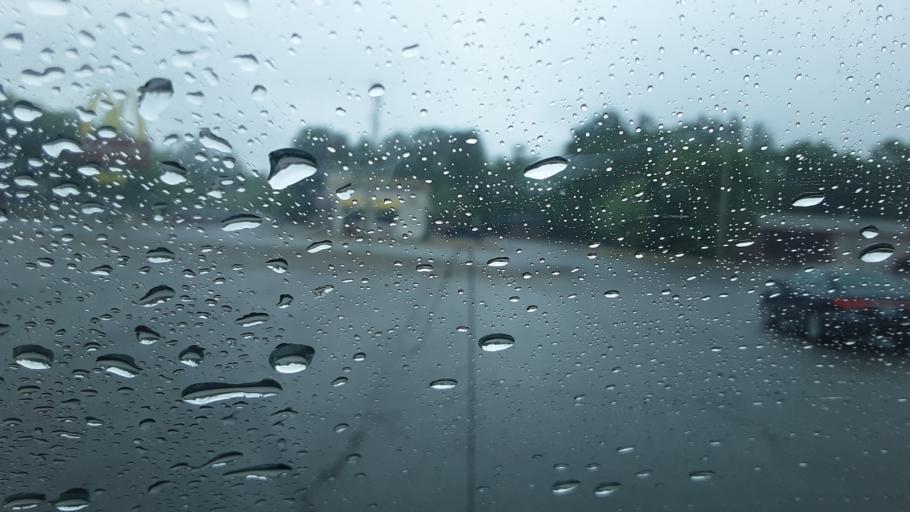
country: US
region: Maine
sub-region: Penobscot County
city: Millinocket
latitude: 45.6568
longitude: -68.6900
